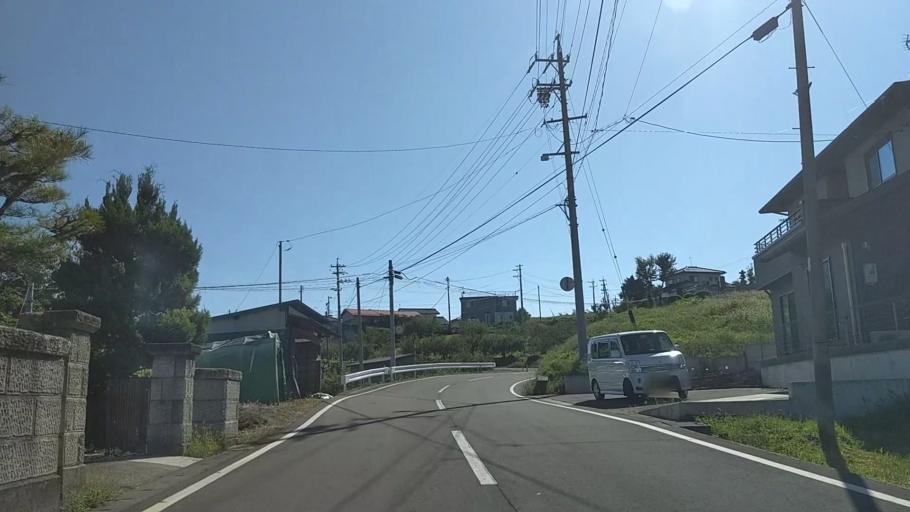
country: JP
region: Nagano
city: Nagano-shi
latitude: 36.5779
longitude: 138.1187
